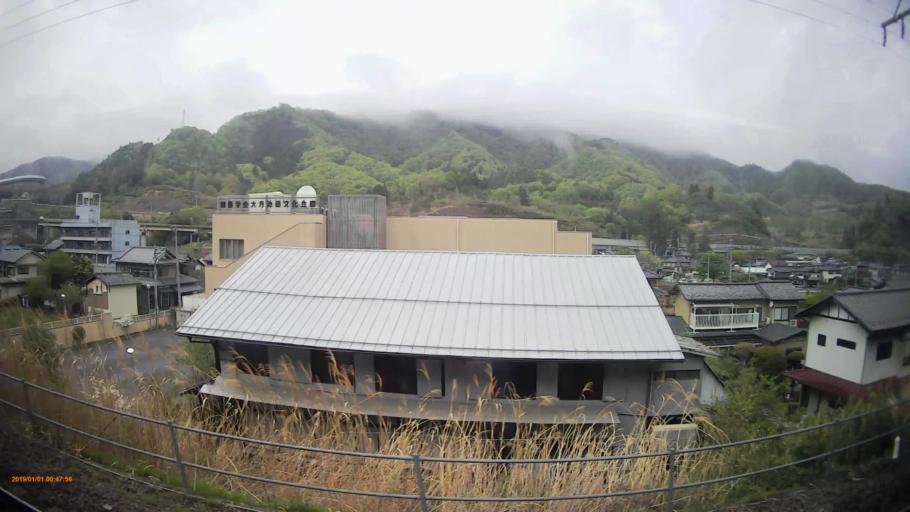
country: JP
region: Yamanashi
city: Otsuki
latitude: 35.6017
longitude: 138.9225
